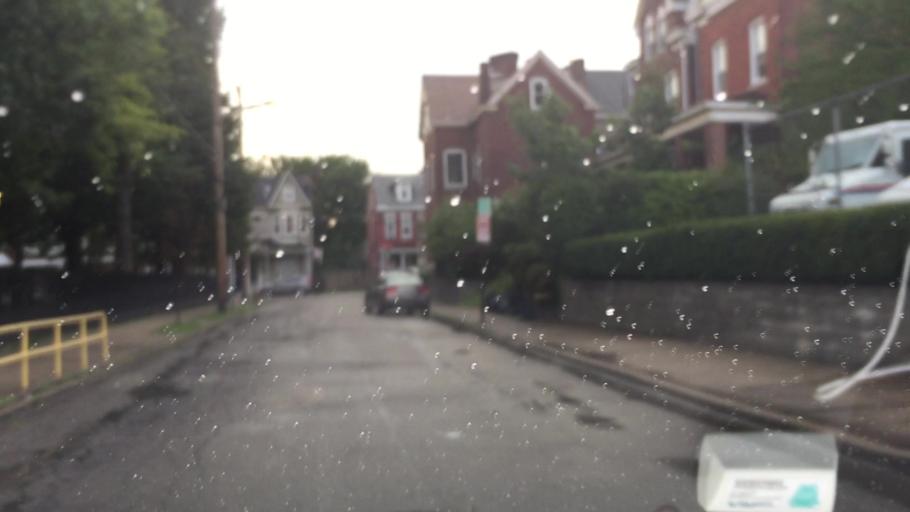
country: US
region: Pennsylvania
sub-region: Allegheny County
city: Bloomfield
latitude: 40.4568
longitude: -79.9418
